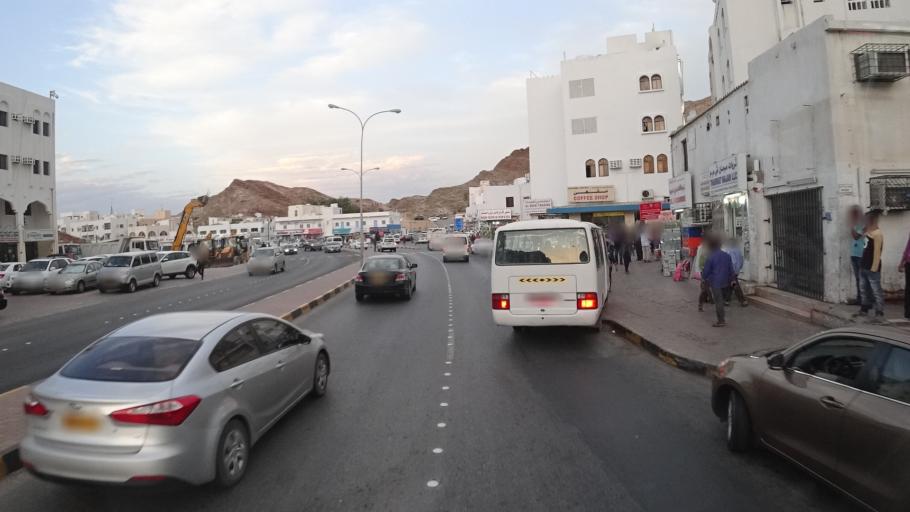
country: OM
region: Muhafazat Masqat
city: Muscat
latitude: 23.5821
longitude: 58.5444
